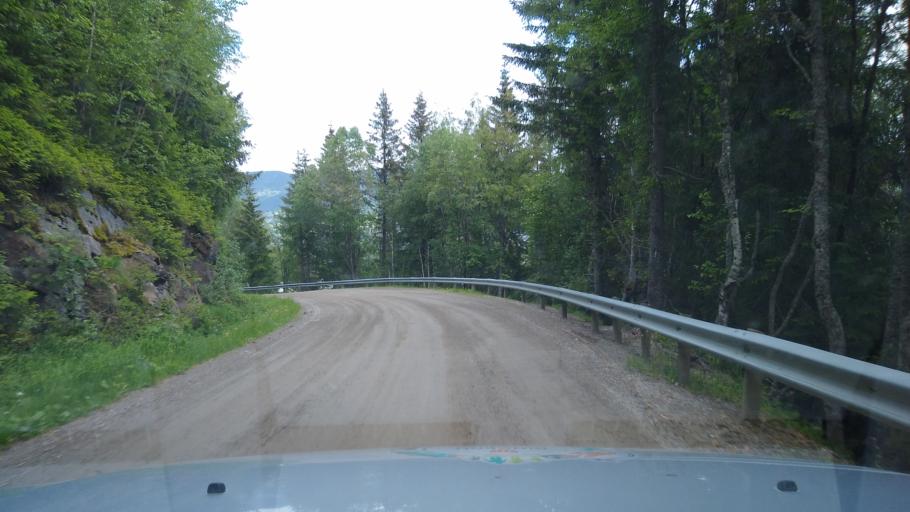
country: NO
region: Oppland
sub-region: Ringebu
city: Ringebu
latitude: 61.5058
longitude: 10.1376
